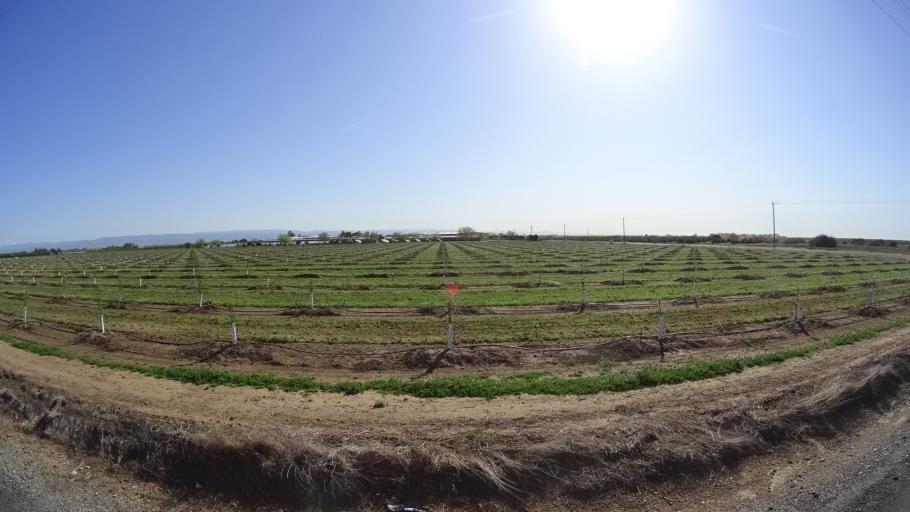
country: US
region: California
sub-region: Glenn County
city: Hamilton City
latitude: 39.7671
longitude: -122.0666
